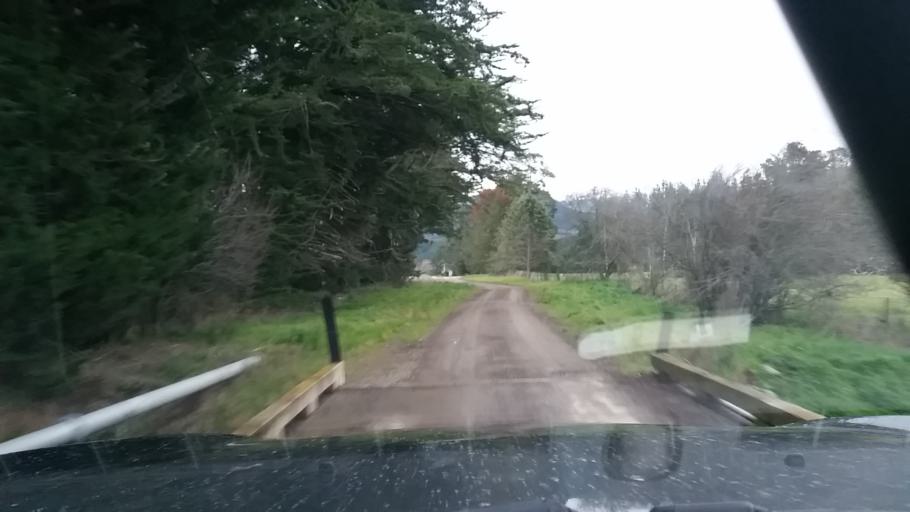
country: NZ
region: Nelson
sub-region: Nelson City
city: Nelson
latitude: -41.5624
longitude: 173.5224
